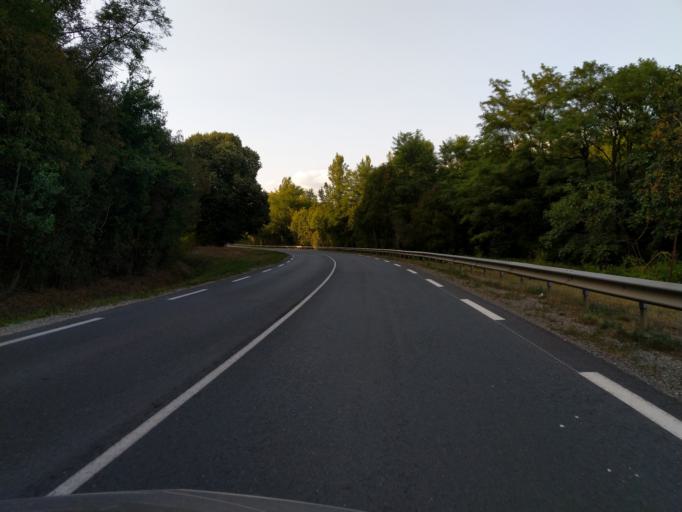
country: FR
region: Midi-Pyrenees
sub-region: Departement du Tarn
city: Realmont
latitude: 43.7874
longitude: 2.1887
